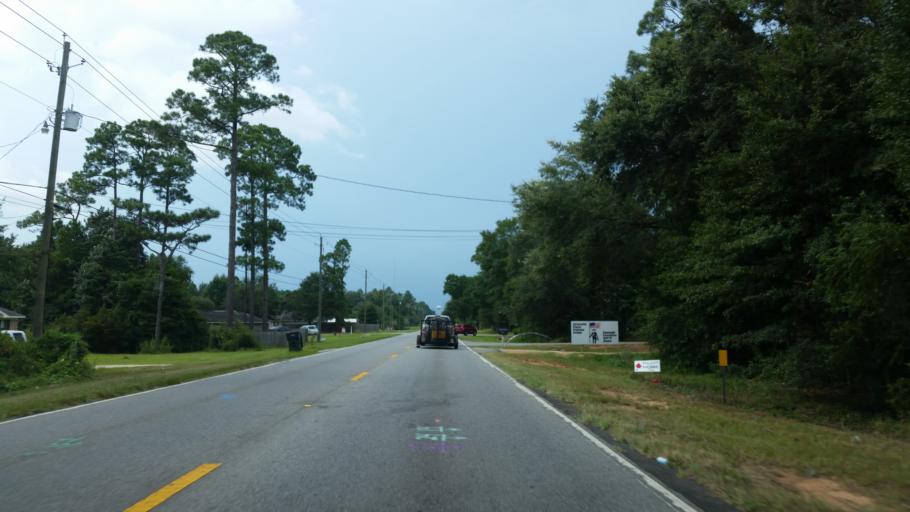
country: US
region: Florida
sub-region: Santa Rosa County
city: Wallace
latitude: 30.6463
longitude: -87.1832
